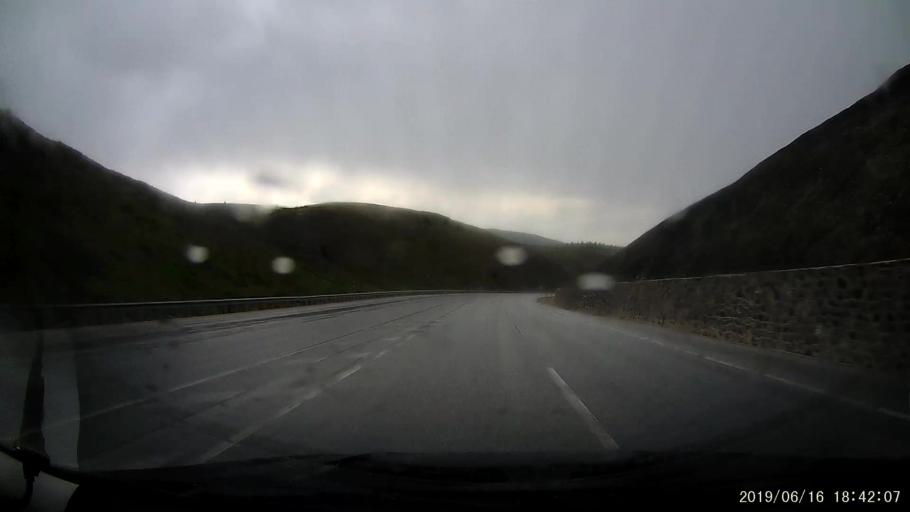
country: TR
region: Erzincan
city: Doganbeyli
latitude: 39.8713
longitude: 39.1160
